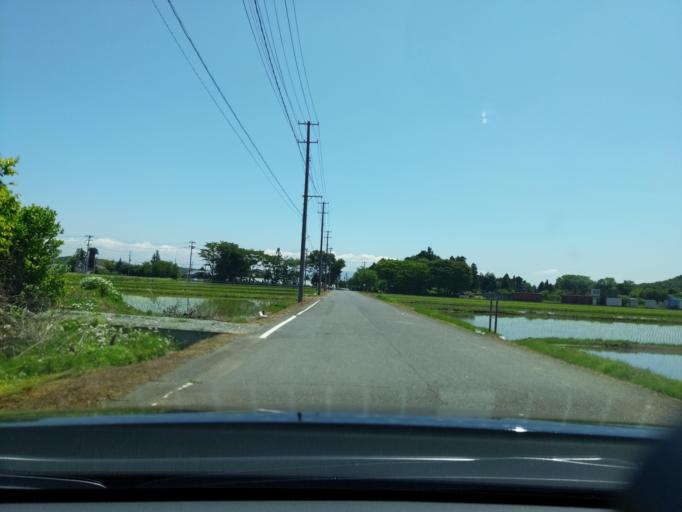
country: JP
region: Fukushima
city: Koriyama
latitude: 37.3923
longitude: 140.2775
